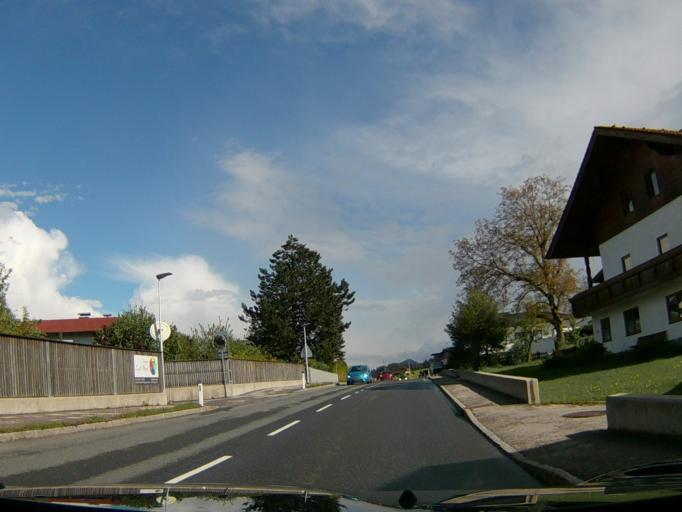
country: AT
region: Salzburg
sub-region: Politischer Bezirk Salzburg-Umgebung
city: Plainfeld
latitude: 47.8587
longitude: 13.1733
